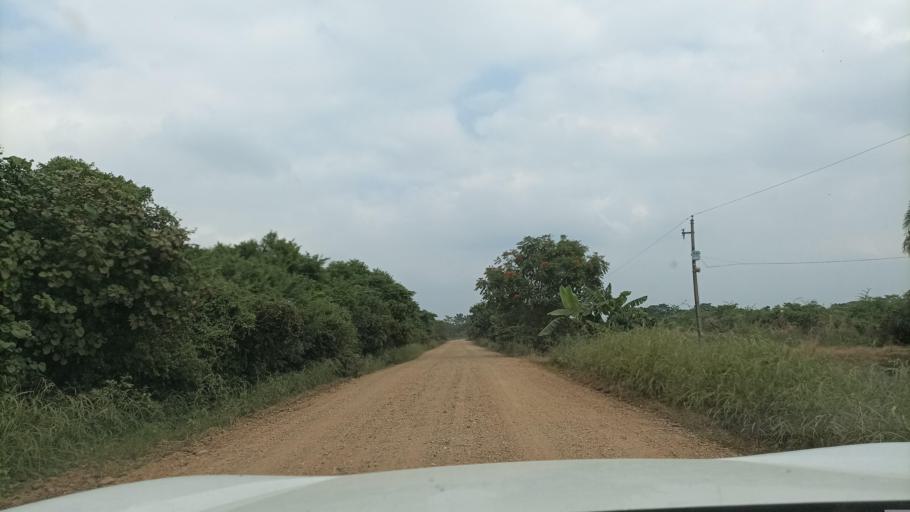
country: MX
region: Veracruz
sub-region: Texistepec
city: San Lorenzo Tenochtitlan
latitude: 17.7831
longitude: -94.7884
